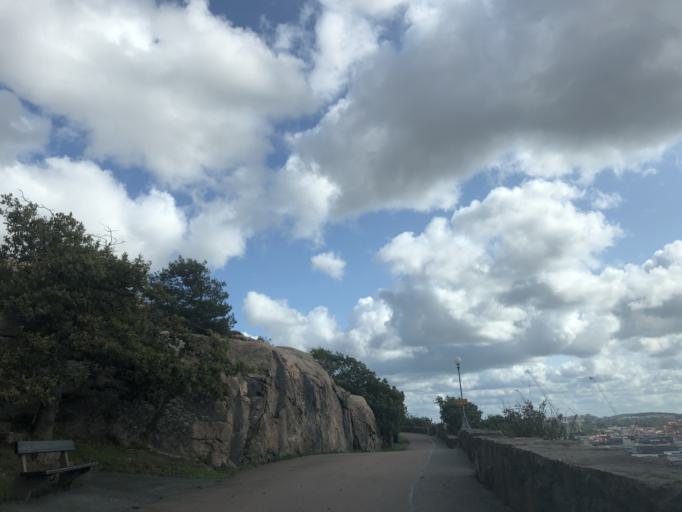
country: SE
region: Vaestra Goetaland
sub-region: Goteborg
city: Majorna
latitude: 57.7139
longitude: 11.9350
